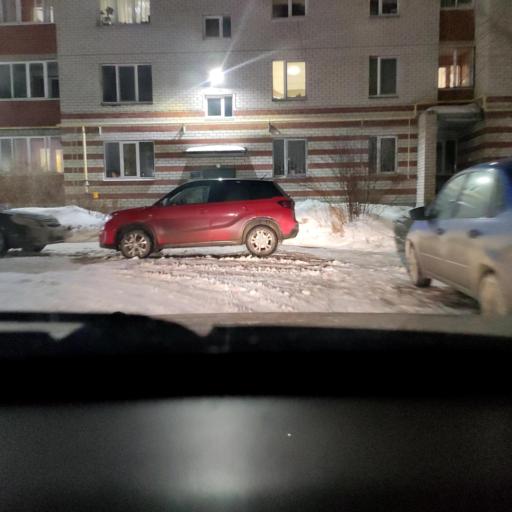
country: RU
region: Perm
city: Gamovo
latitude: 57.8727
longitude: 56.0953
